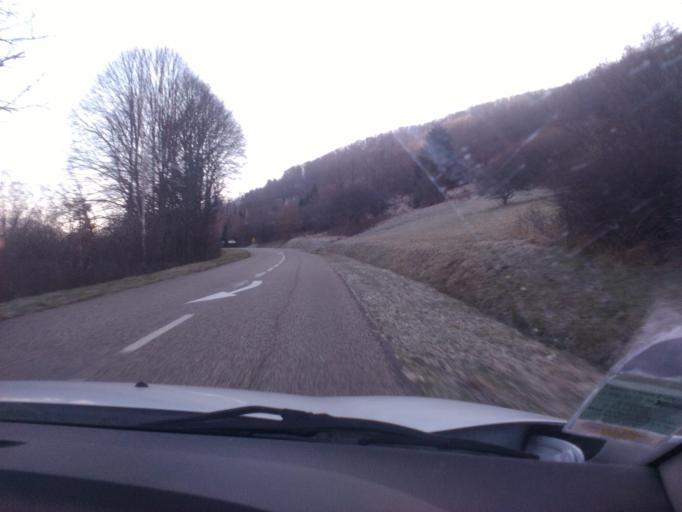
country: FR
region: Alsace
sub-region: Departement du Bas-Rhin
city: Russ
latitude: 48.4857
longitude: 7.2422
